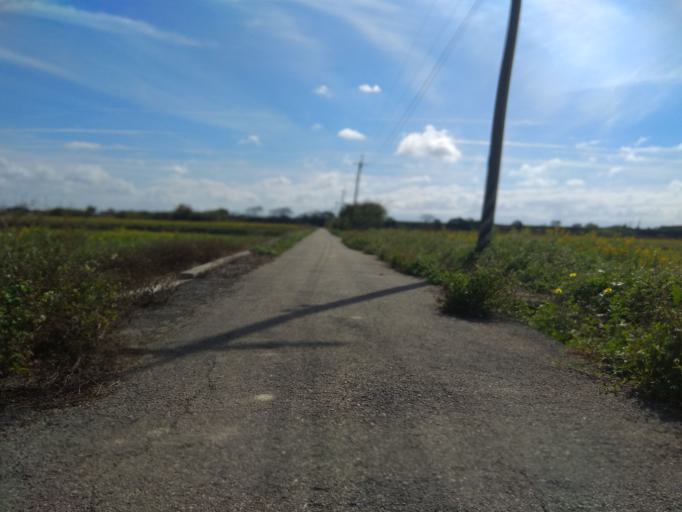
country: TW
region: Taiwan
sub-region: Hsinchu
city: Zhubei
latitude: 25.0177
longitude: 121.0651
